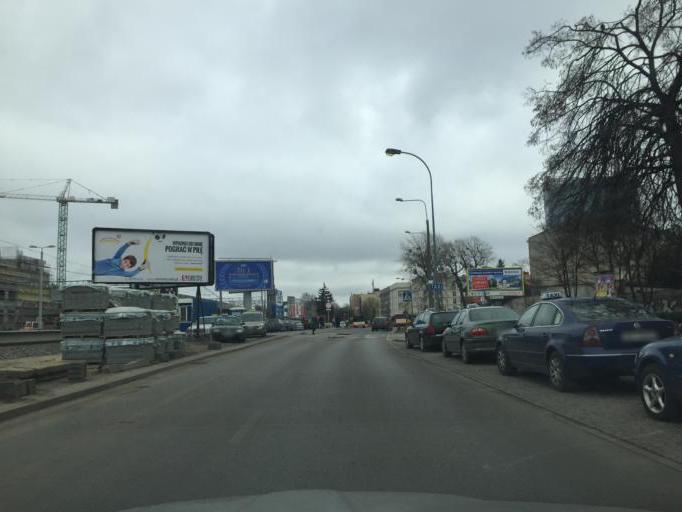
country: PL
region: Pomeranian Voivodeship
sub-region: Gdansk
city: Gdansk
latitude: 54.3827
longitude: 18.6026
